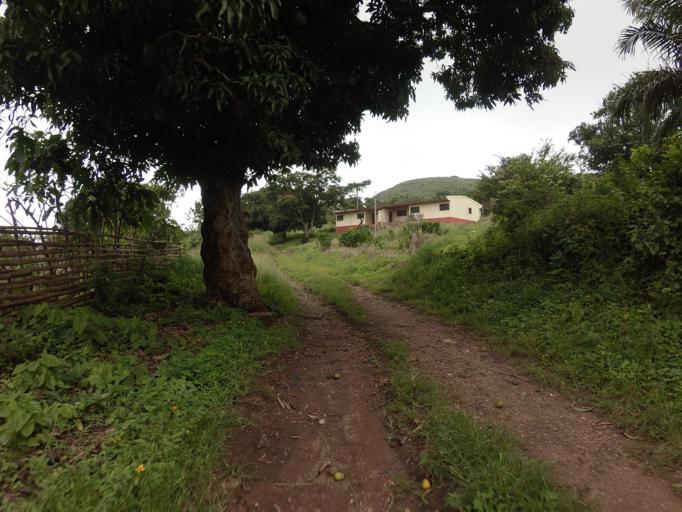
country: GH
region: Volta
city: Kpandu
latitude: 6.8520
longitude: 0.4347
